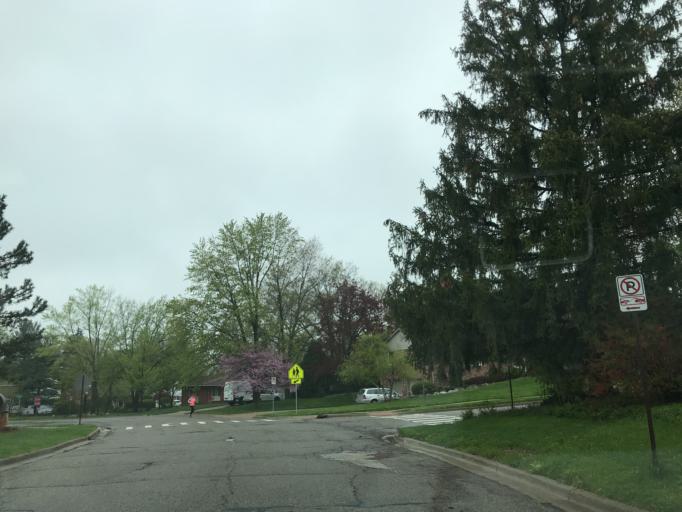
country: US
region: Michigan
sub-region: Washtenaw County
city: Ann Arbor
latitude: 42.2560
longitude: -83.7192
